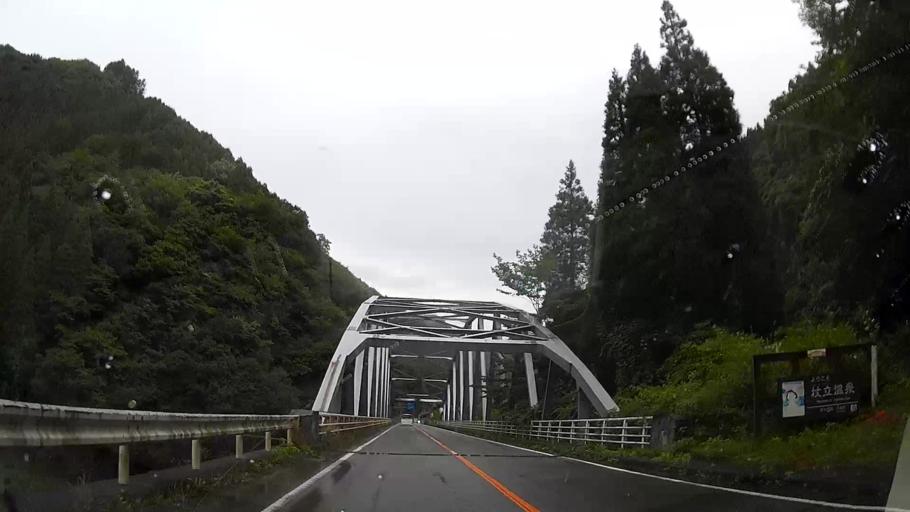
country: JP
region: Oita
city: Tsukawaki
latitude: 33.1702
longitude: 131.0383
